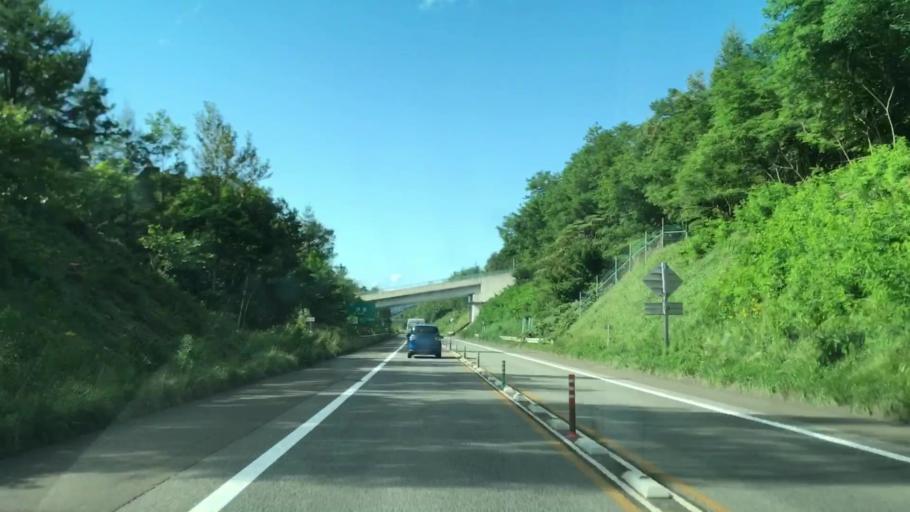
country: JP
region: Hokkaido
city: Date
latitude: 42.4716
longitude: 140.9054
